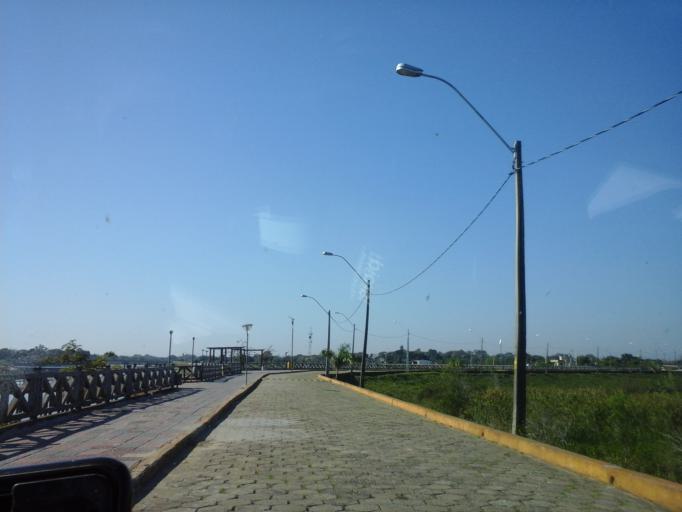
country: PY
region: Neembucu
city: Pilar
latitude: -26.8529
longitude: -58.3037
